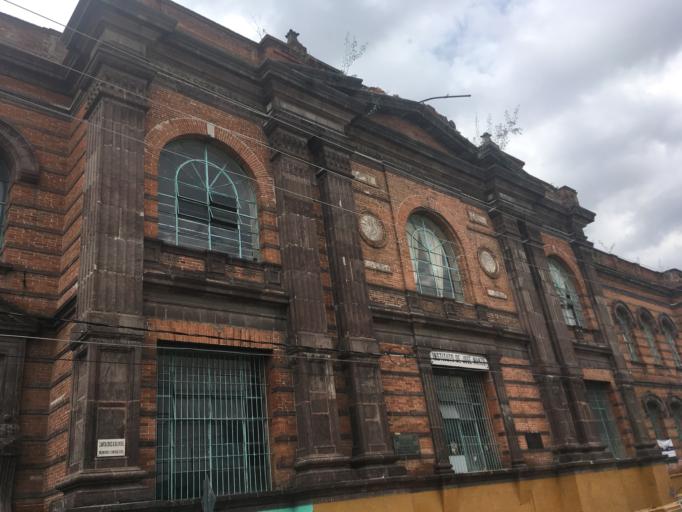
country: MX
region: Puebla
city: Puebla
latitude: 19.0463
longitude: -98.2061
